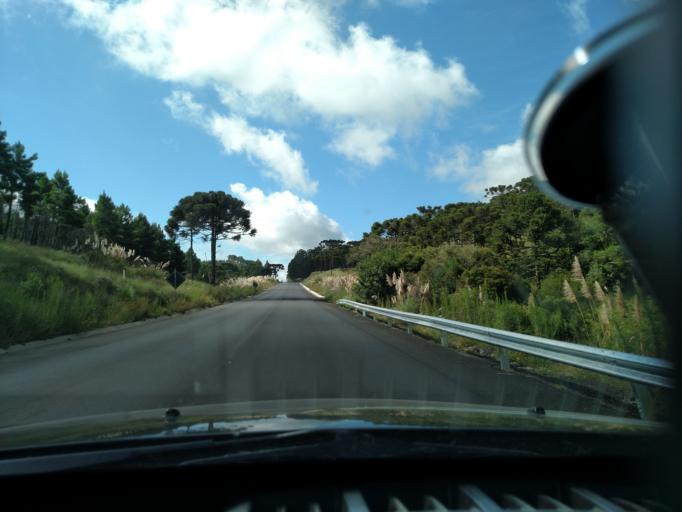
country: BR
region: Santa Catarina
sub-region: Lages
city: Lages
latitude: -27.9676
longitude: -50.0987
